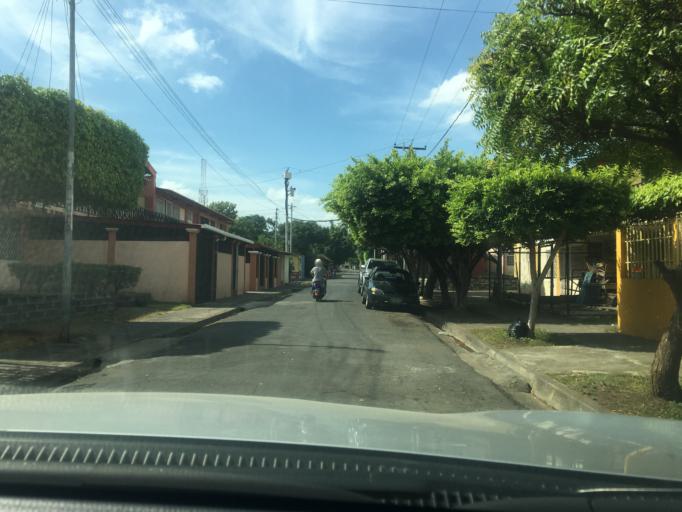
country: NI
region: Managua
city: Managua
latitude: 12.1583
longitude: -86.2759
